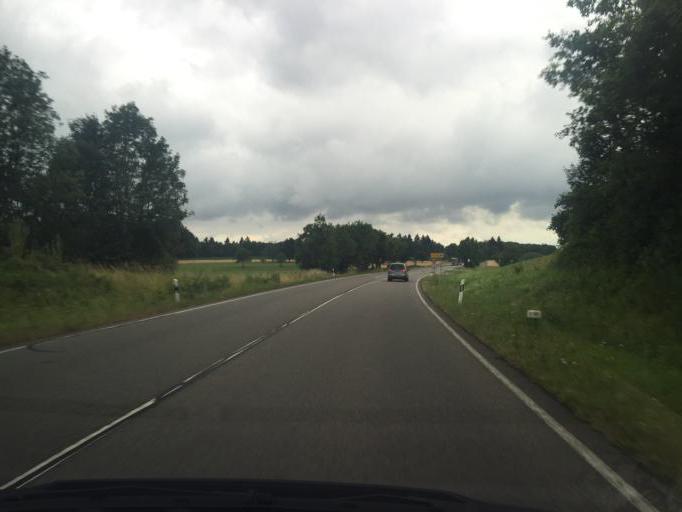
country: DE
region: Baden-Wuerttemberg
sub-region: Karlsruhe Region
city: Bretten
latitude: 48.9995
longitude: 8.7179
